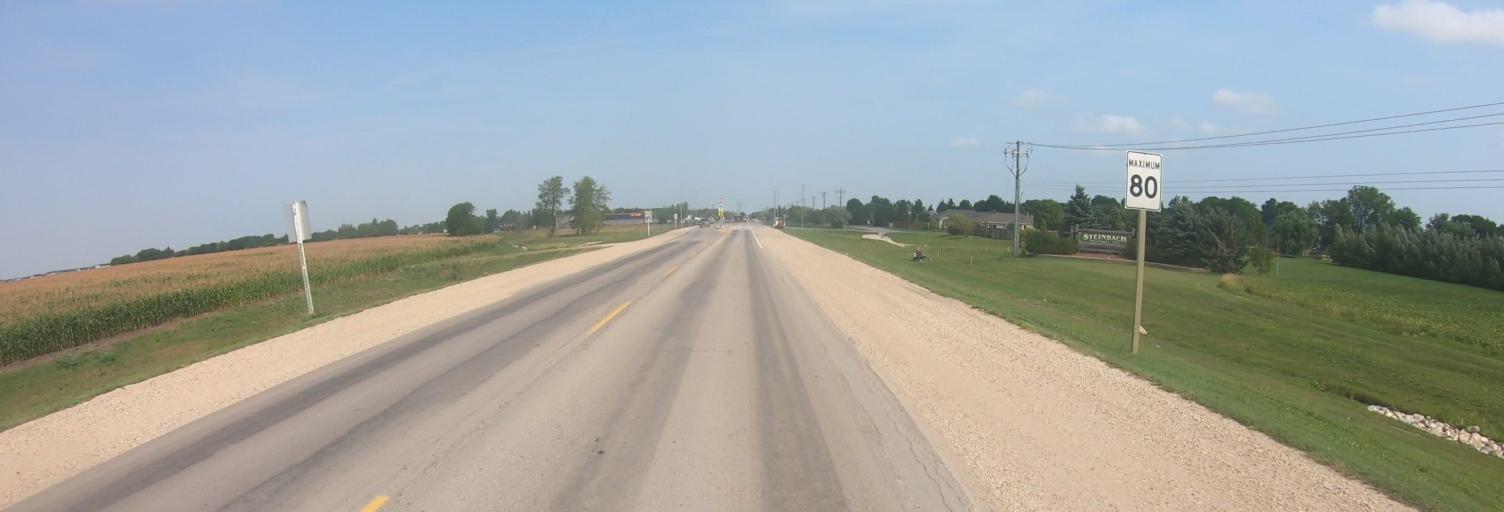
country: CA
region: Manitoba
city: Steinbach
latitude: 49.5078
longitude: -96.6913
